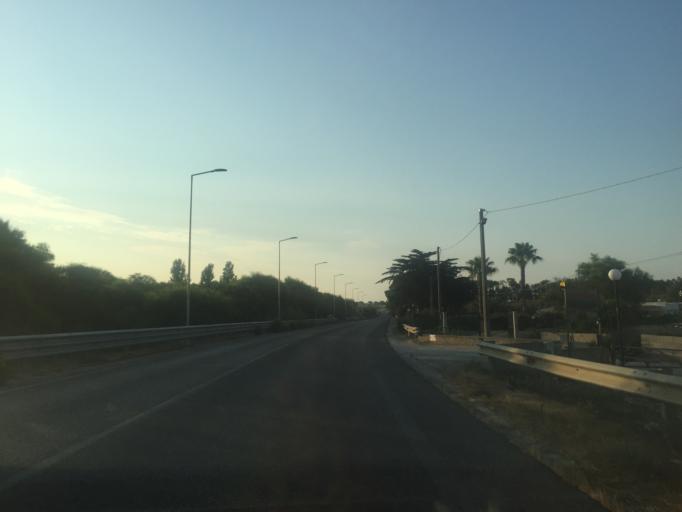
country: IT
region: Sicily
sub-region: Ragusa
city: Cava d'Aliga
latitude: 36.7231
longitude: 14.7498
